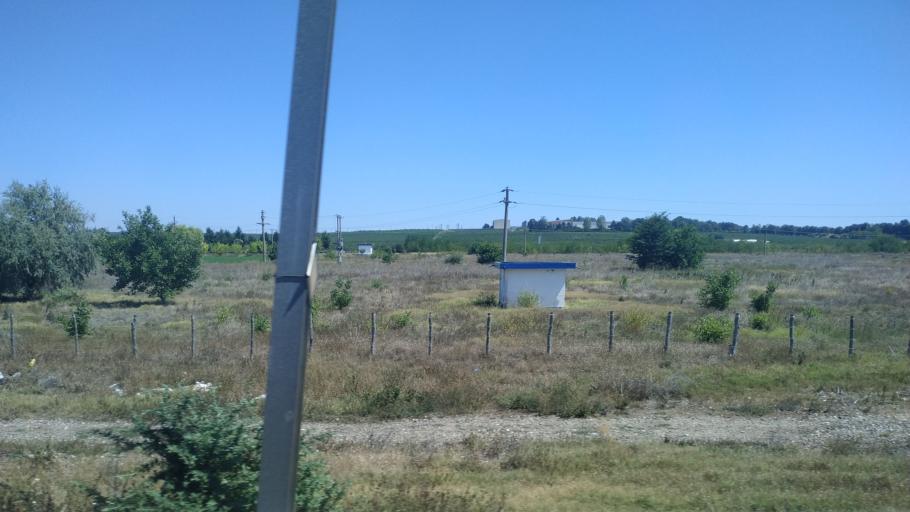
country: RO
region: Constanta
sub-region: Oras Murfatlar
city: Murfatlar
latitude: 44.1835
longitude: 28.3979
